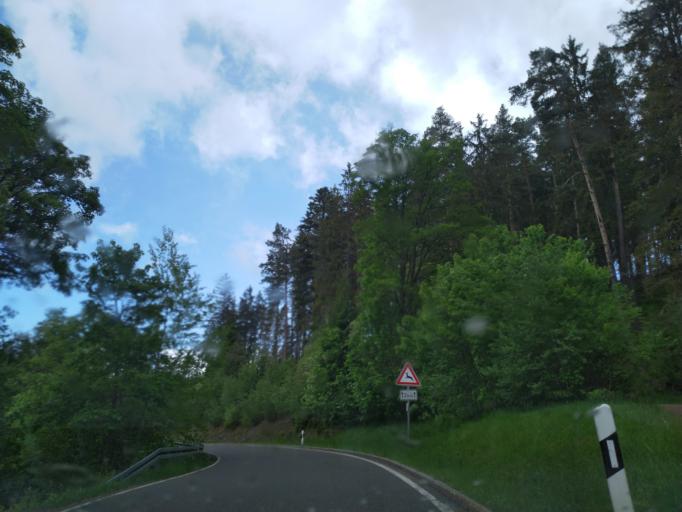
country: DE
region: Baden-Wuerttemberg
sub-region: Freiburg Region
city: Friedenweiler
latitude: 47.9200
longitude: 8.2583
